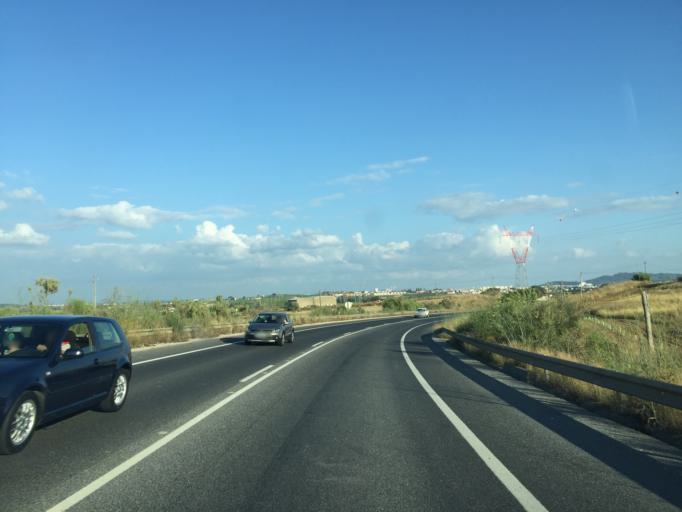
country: PT
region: Lisbon
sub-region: Alenquer
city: Alenquer
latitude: 39.0627
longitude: -8.9966
